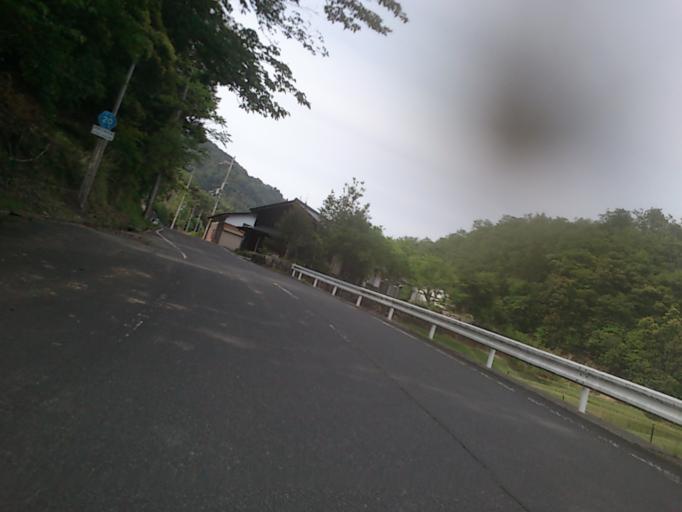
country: JP
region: Hyogo
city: Toyooka
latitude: 35.5968
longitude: 134.9817
